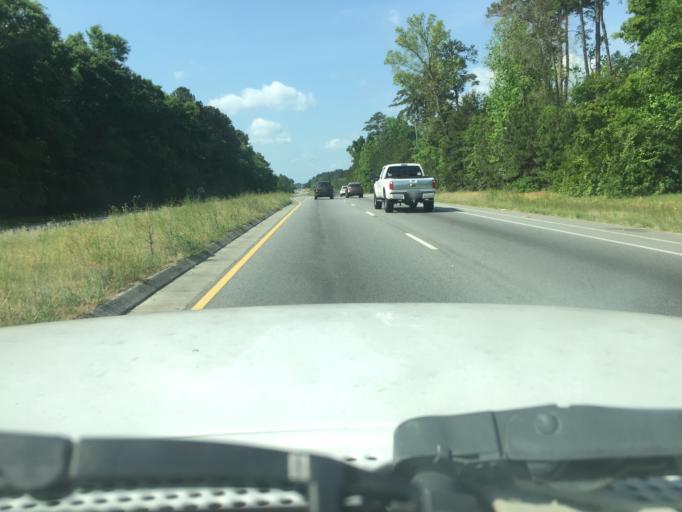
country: US
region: Georgia
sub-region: Chatham County
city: Georgetown
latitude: 32.0227
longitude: -81.2267
